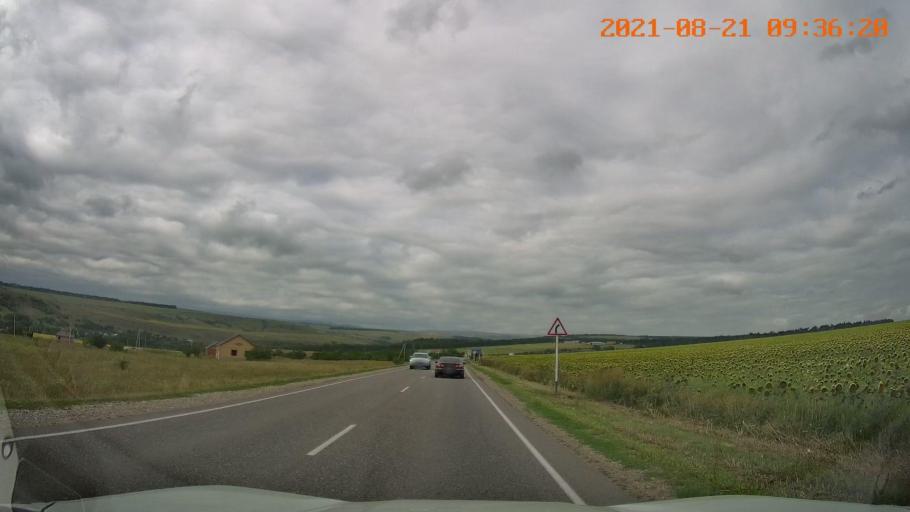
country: RU
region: Stavropol'skiy
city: Yutsa
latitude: 43.9817
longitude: 42.9512
